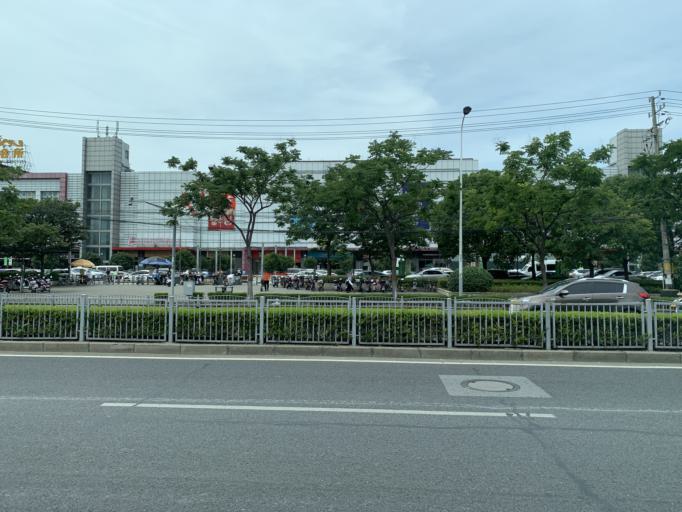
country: CN
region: Shanghai Shi
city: Kangqiao
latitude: 31.1562
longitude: 121.5607
